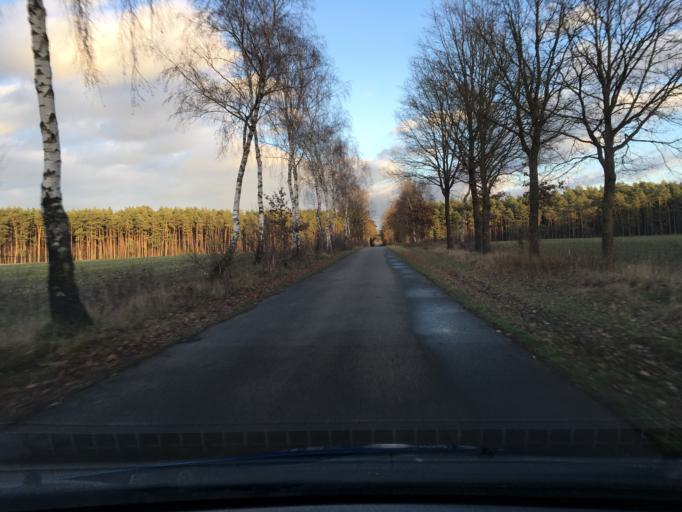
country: DE
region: Lower Saxony
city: Soderstorf
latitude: 53.1098
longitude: 10.1476
